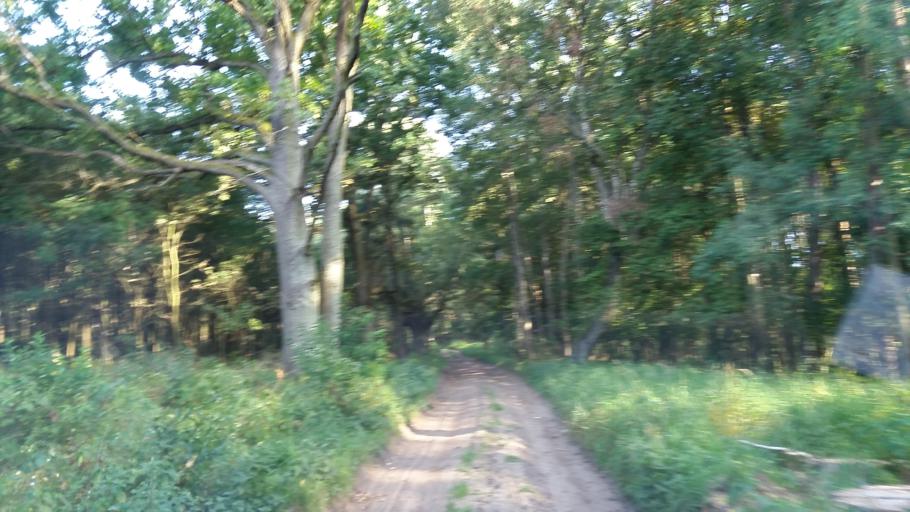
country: PL
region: West Pomeranian Voivodeship
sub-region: Powiat choszczenski
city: Recz
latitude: 53.1982
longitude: 15.5425
